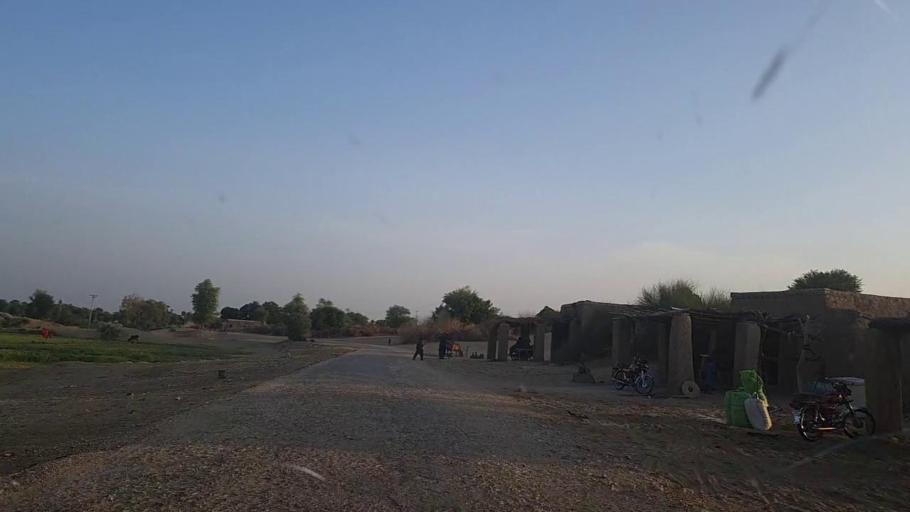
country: PK
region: Sindh
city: Khanpur
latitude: 27.6261
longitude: 69.4444
